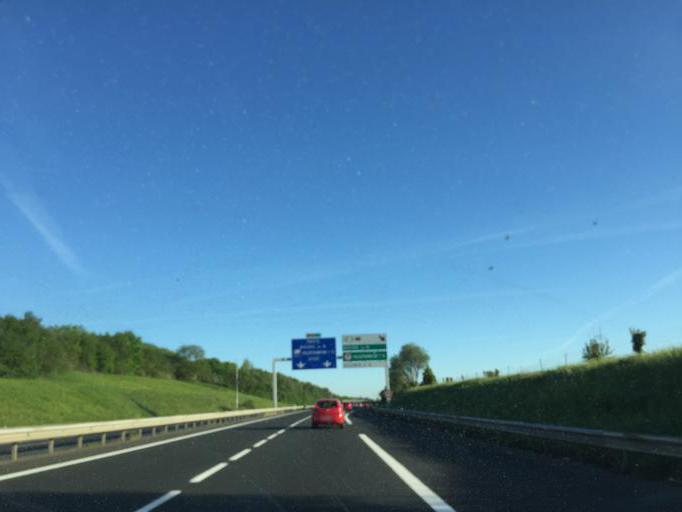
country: FR
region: Rhone-Alpes
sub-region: Departement du Rhone
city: Sathonay-Village
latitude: 45.8505
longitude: 4.9107
